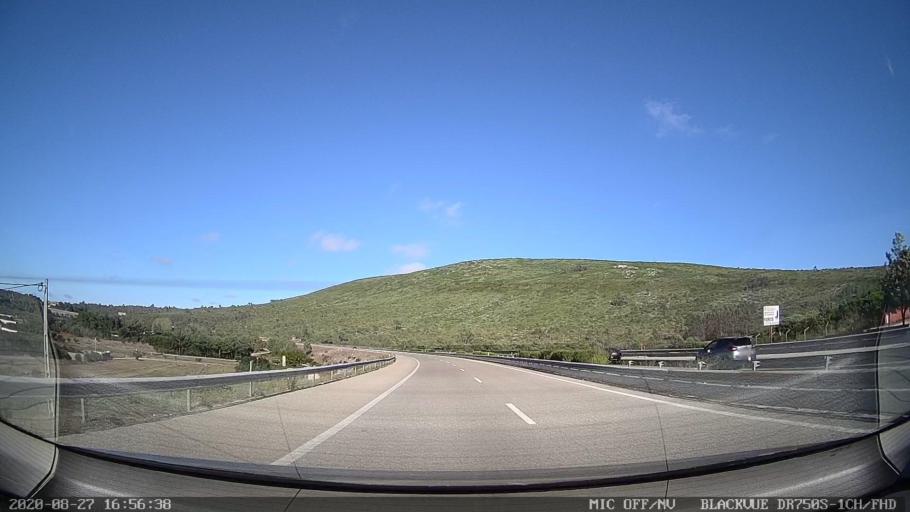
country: PT
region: Santarem
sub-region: Alcanena
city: Alcanena
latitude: 39.5281
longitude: -8.6653
